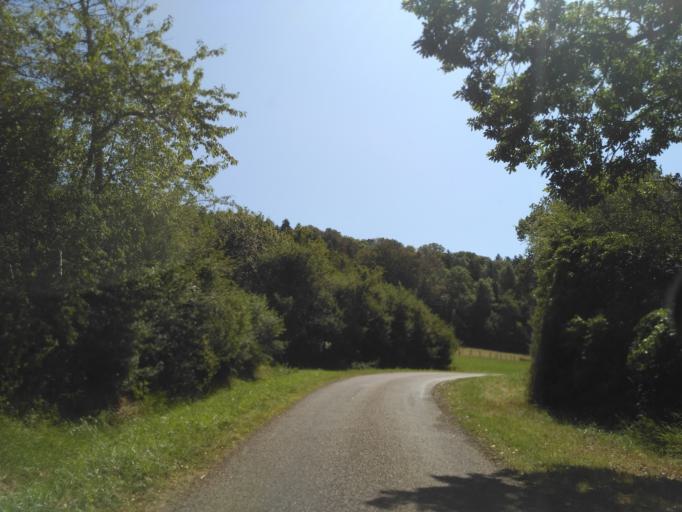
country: FR
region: Franche-Comte
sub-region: Departement de la Haute-Saone
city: Villersexel
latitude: 47.5030
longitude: 6.5279
